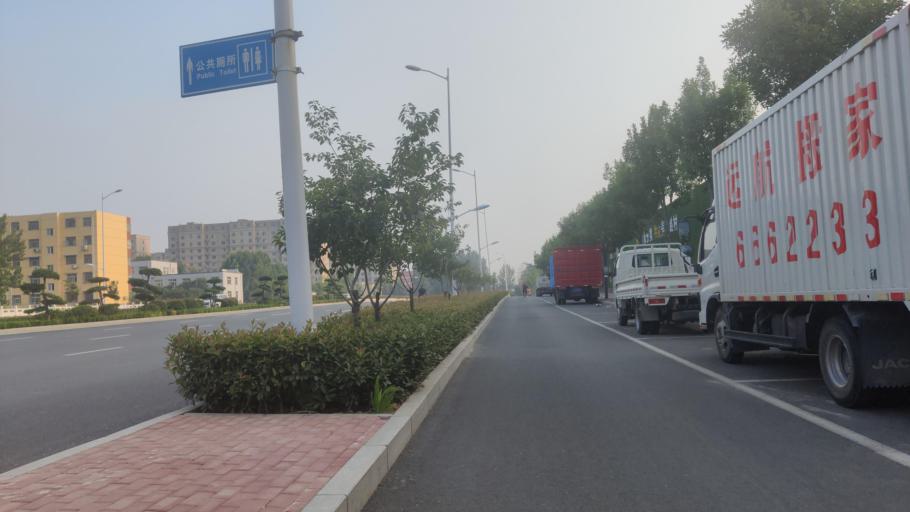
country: CN
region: Henan Sheng
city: Zhongyuanlu
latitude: 35.7587
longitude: 115.0830
